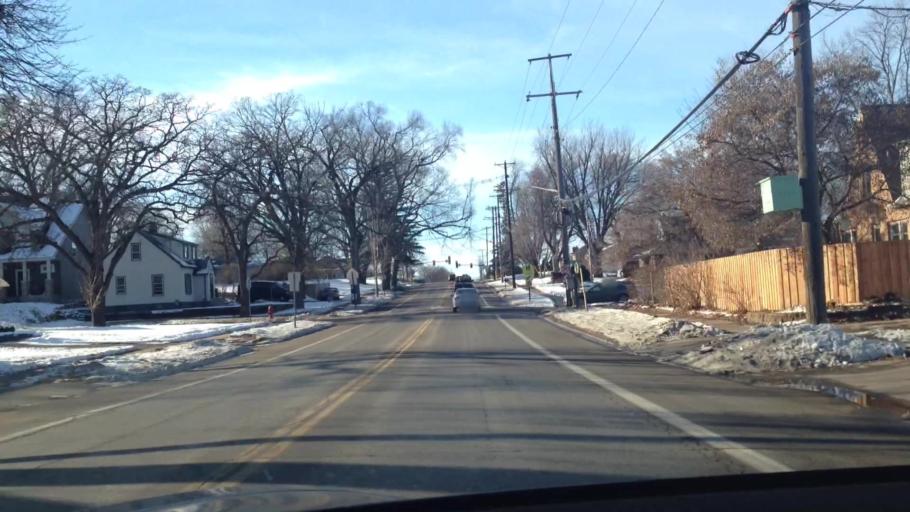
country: US
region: Minnesota
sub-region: Hennepin County
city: Saint Louis Park
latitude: 44.9495
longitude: -93.3776
